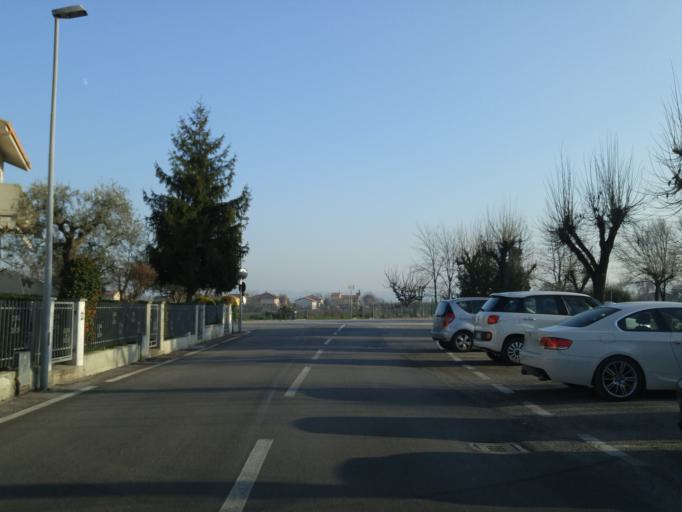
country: IT
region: The Marches
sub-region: Provincia di Pesaro e Urbino
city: Lucrezia
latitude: 43.7757
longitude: 12.9414
